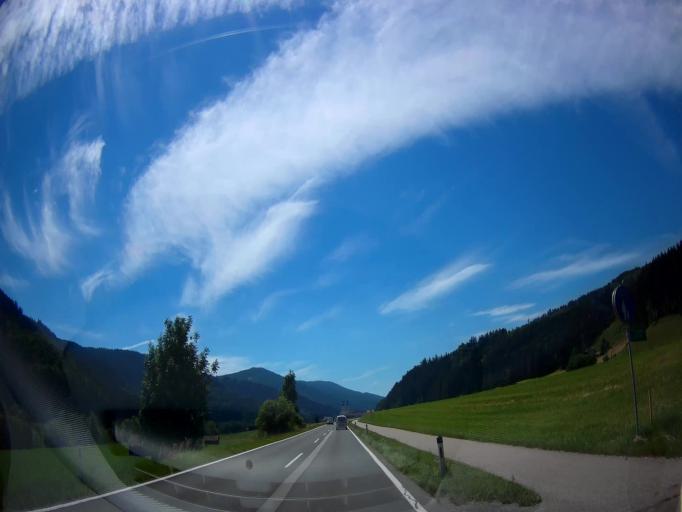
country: AT
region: Carinthia
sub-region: Politischer Bezirk Sankt Veit an der Glan
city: Gurk
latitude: 46.8826
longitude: 14.3083
